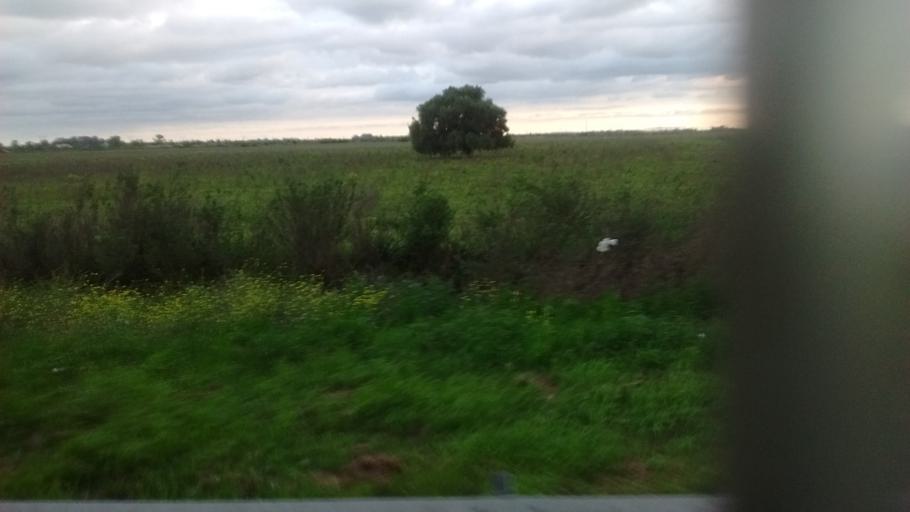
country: AR
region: Santa Fe
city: Funes
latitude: -32.9277
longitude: -60.7719
